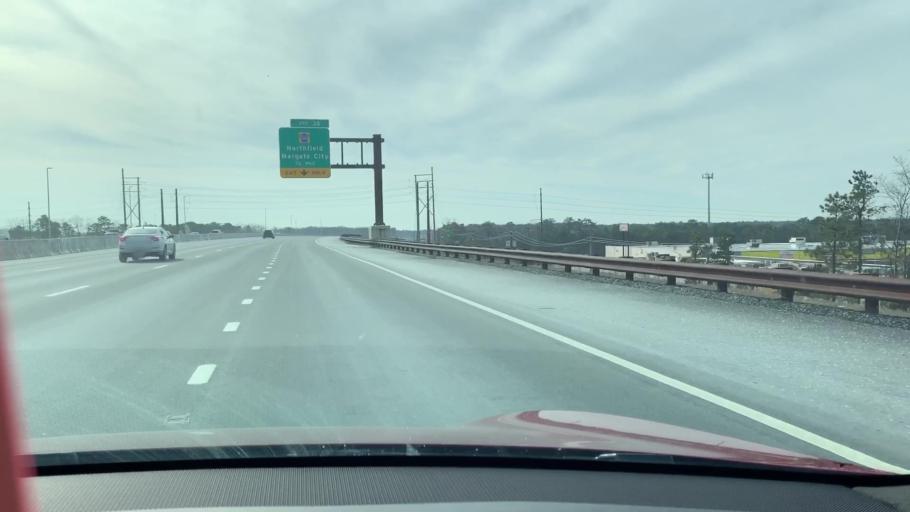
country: US
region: New Jersey
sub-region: Atlantic County
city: Northfield
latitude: 39.4042
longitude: -74.5580
